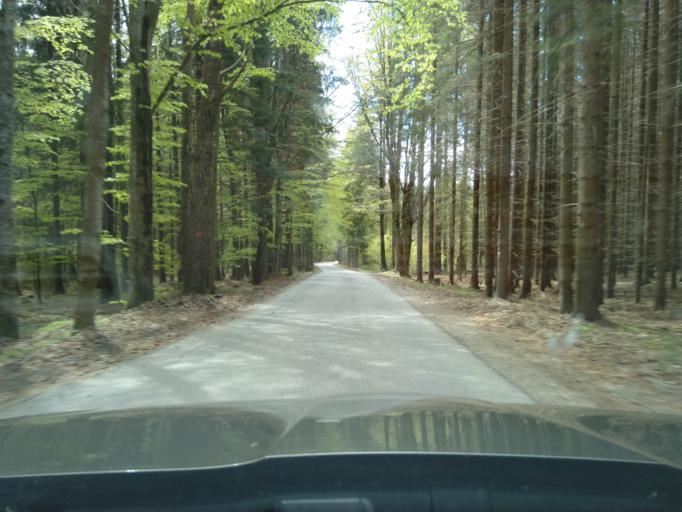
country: CZ
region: Jihocesky
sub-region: Okres Prachatice
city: Borova Lada
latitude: 49.0001
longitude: 13.6897
